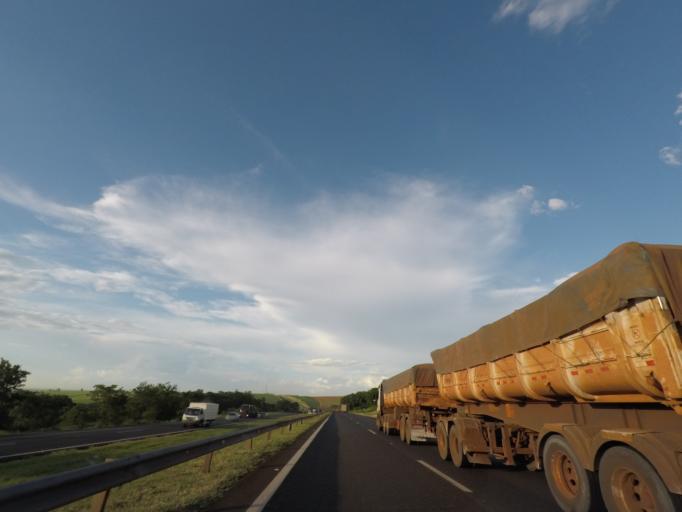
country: BR
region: Sao Paulo
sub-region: Ituverava
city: Ituverava
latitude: -20.2937
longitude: -47.7984
